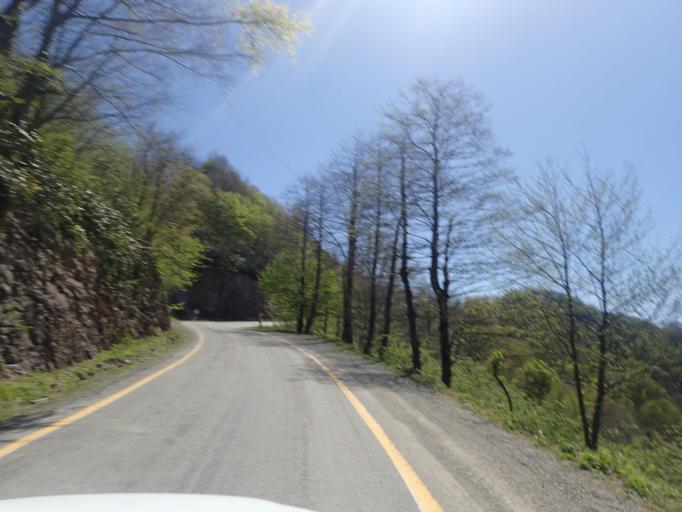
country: TR
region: Ordu
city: Kabaduz
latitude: 40.7944
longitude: 37.9142
